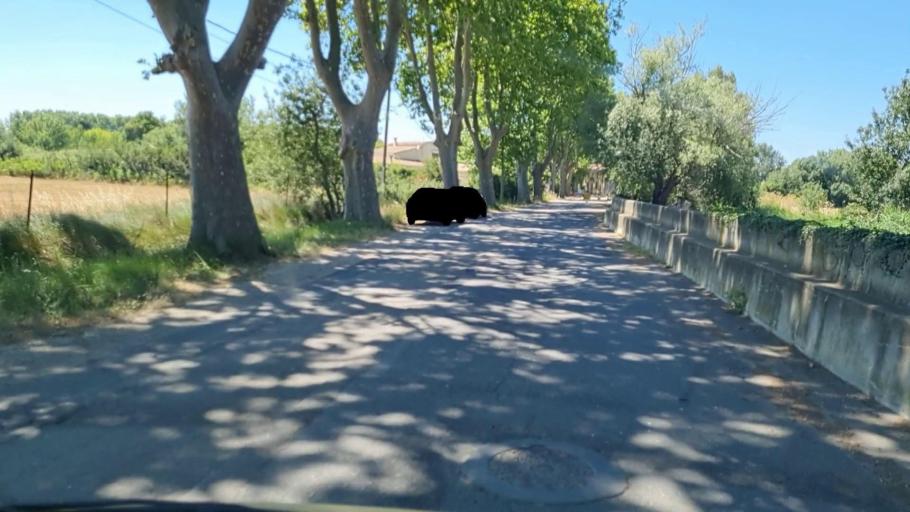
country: FR
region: Languedoc-Roussillon
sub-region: Departement du Gard
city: Le Cailar
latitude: 43.6716
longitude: 4.2411
